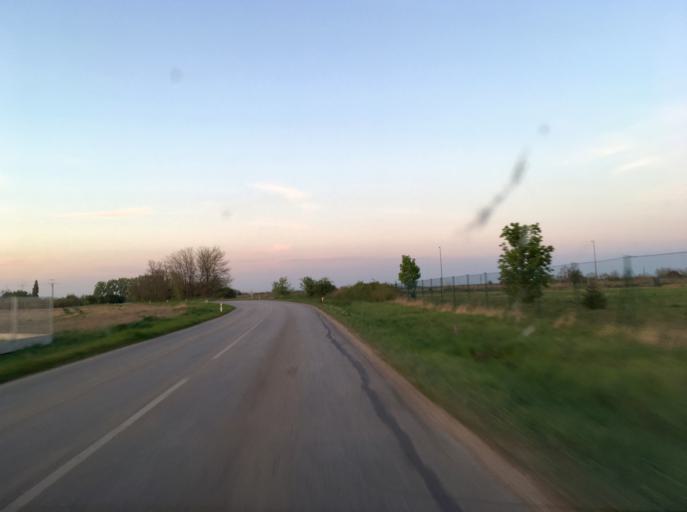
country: SK
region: Nitriansky
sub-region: Okres Nove Zamky
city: Nove Zamky
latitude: 47.9374
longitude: 18.1272
